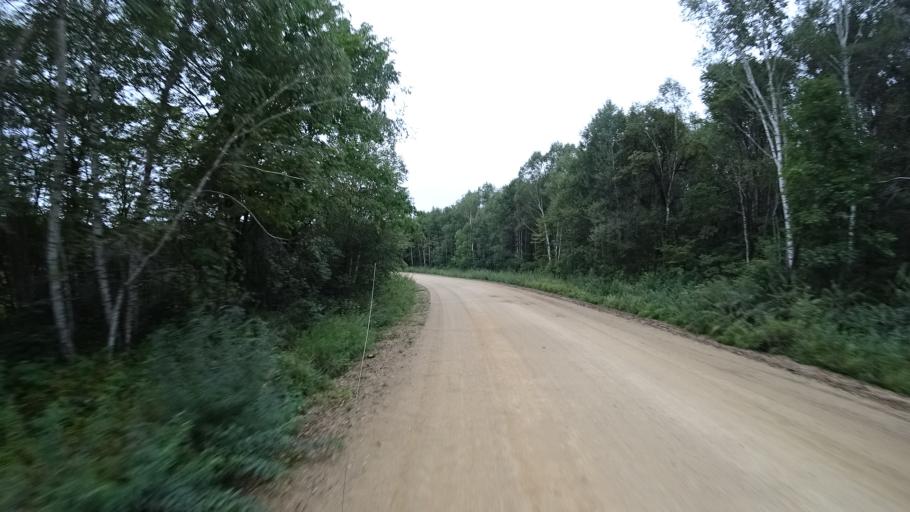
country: RU
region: Primorskiy
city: Rettikhovka
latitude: 44.1805
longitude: 132.8741
